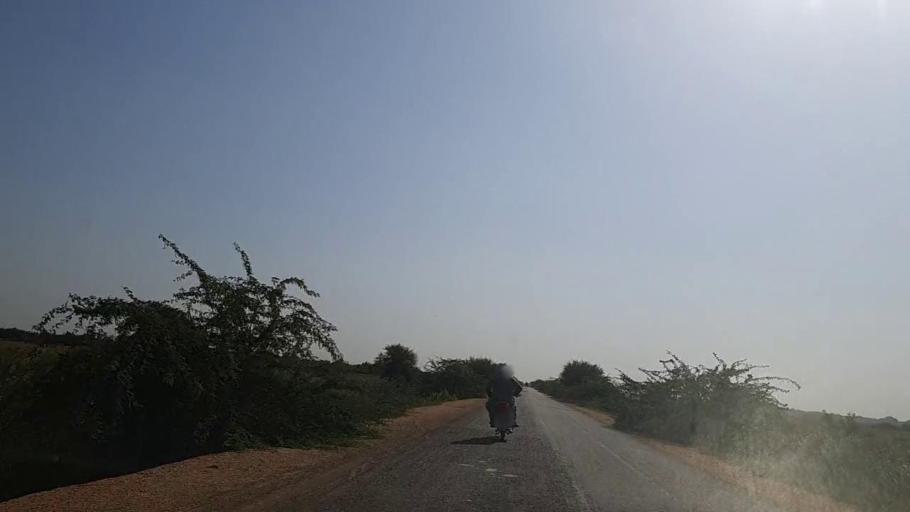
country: PK
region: Sindh
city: Mirpur Batoro
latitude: 24.5871
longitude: 68.2910
